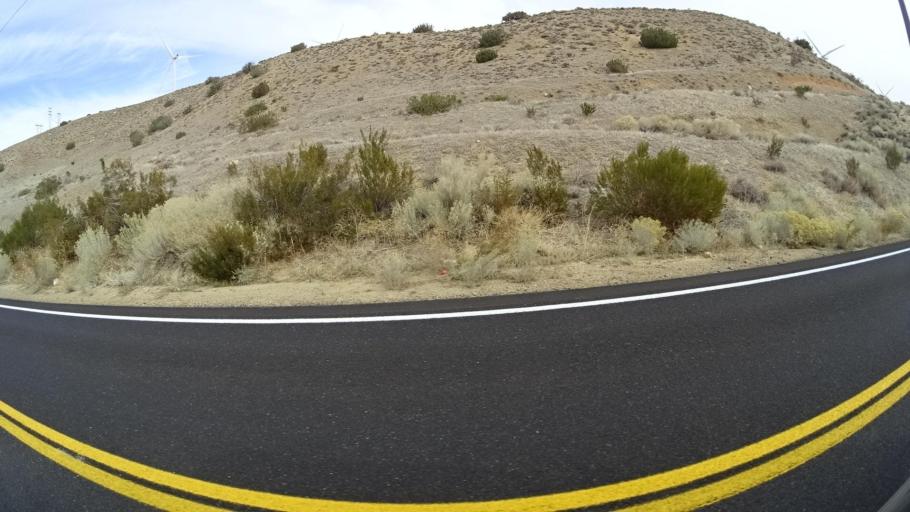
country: US
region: California
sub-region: Kern County
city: Tehachapi
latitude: 35.0502
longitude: -118.3270
